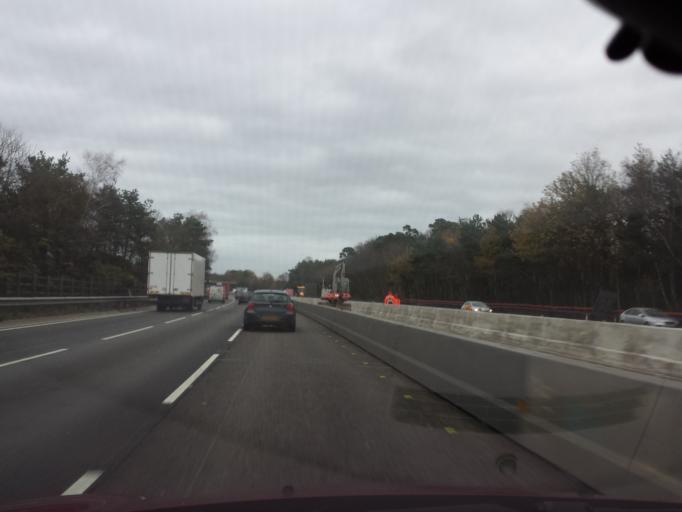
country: GB
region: England
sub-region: Surrey
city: Chobham
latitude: 51.3784
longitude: -0.5951
